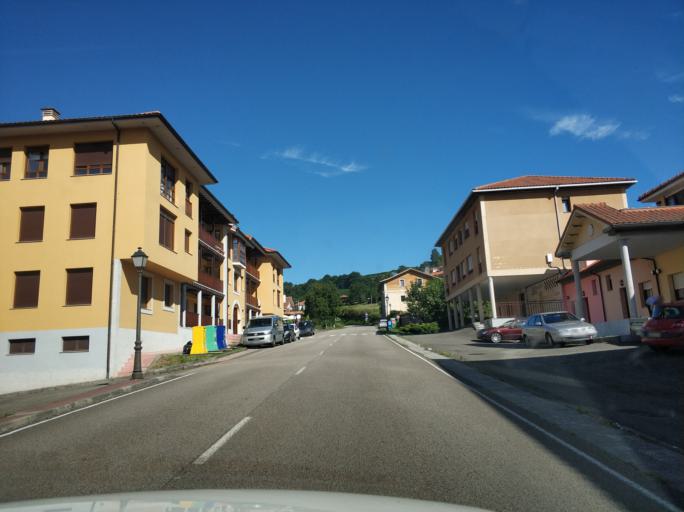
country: ES
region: Asturias
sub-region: Province of Asturias
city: Cudillero
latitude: 43.5626
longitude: -6.2316
